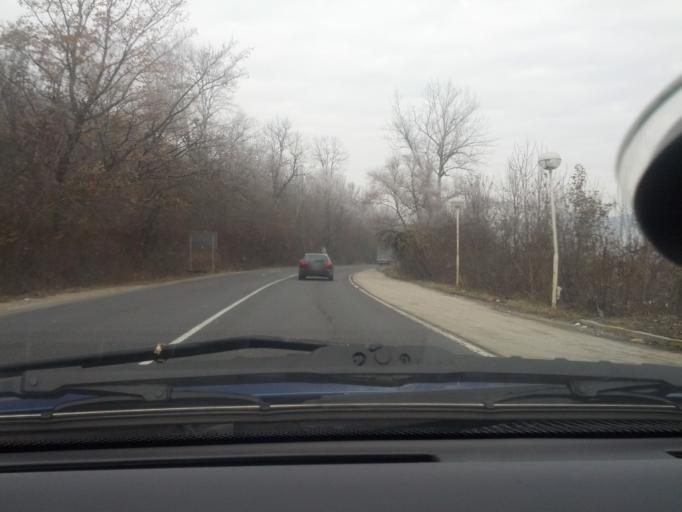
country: BG
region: Sofiya
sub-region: Obshtina Botevgrad
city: Botevgrad
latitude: 42.9557
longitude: 23.7627
